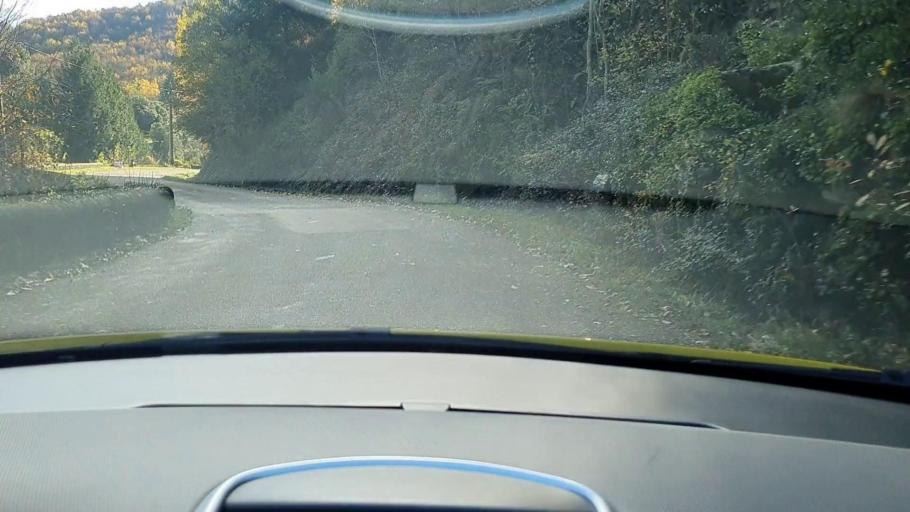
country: FR
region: Languedoc-Roussillon
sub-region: Departement du Gard
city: Valleraugue
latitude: 44.1719
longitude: 3.6456
